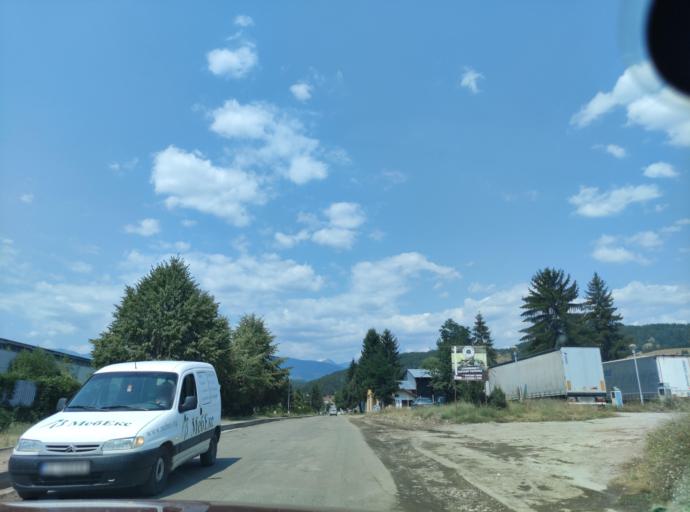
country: BG
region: Blagoevgrad
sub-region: Obshtina Belitsa
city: Belitsa
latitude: 41.9416
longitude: 23.5669
